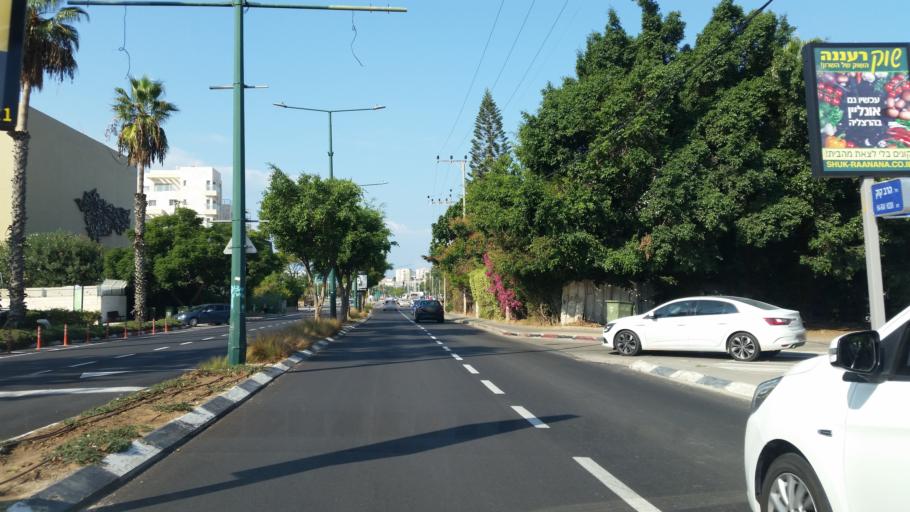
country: IL
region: Tel Aviv
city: Herzliyya
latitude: 32.1631
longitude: 34.8299
